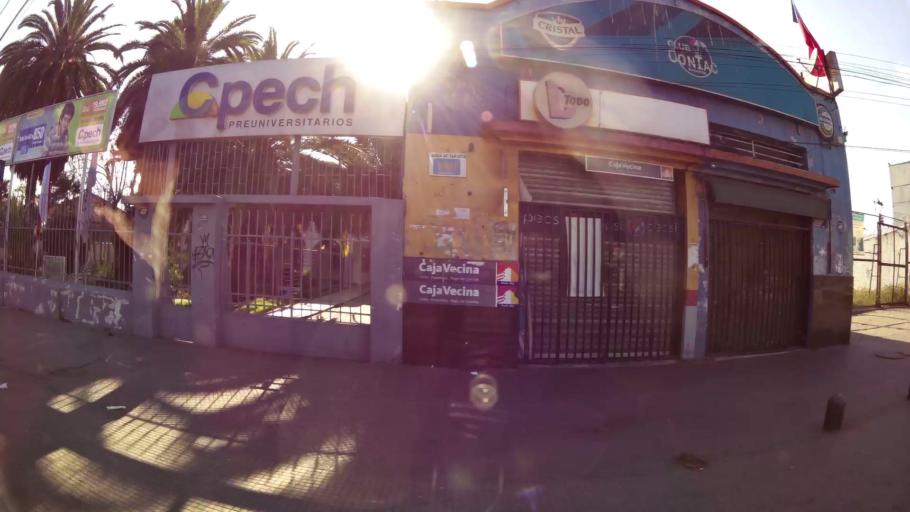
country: CL
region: Santiago Metropolitan
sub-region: Provincia de Santiago
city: Santiago
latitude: -33.3968
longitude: -70.6705
